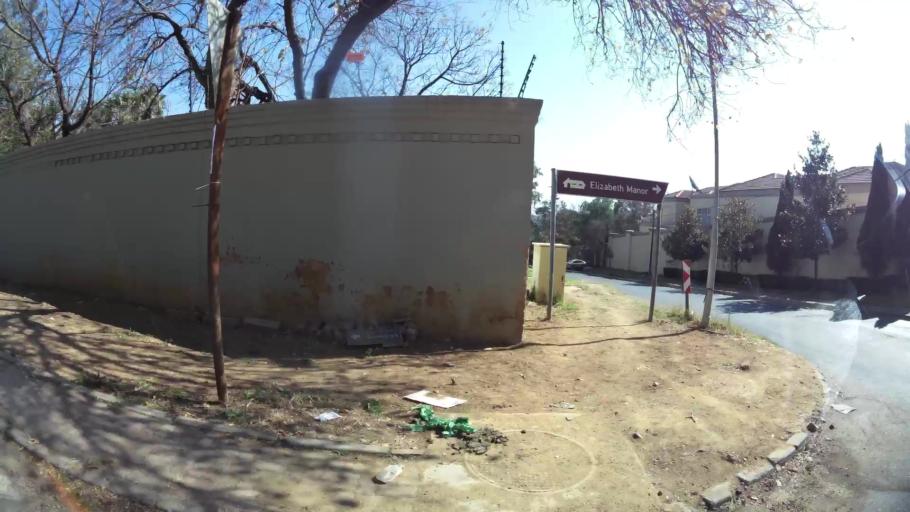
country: ZA
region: Gauteng
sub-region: City of Johannesburg Metropolitan Municipality
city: Johannesburg
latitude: -26.1084
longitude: 28.0427
